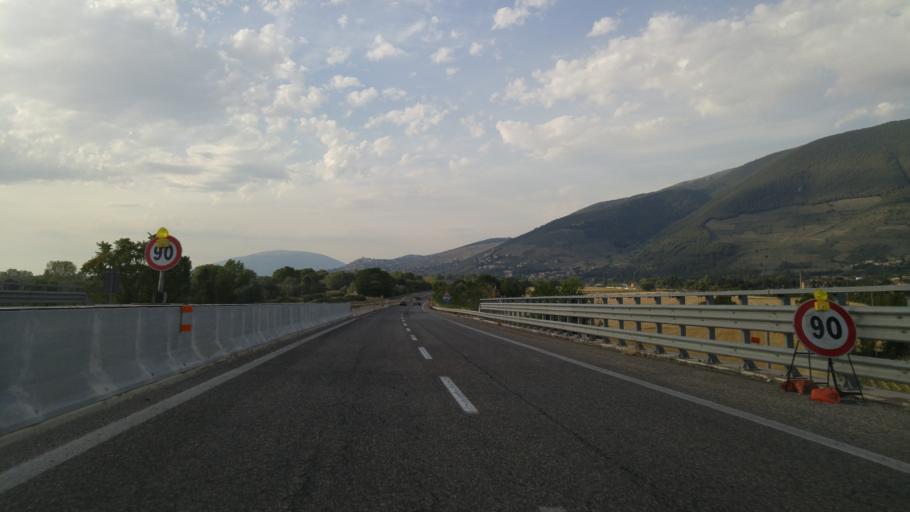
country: IT
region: Umbria
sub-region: Provincia di Perugia
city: Campello sul Clitunno
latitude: 42.8127
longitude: 12.7577
